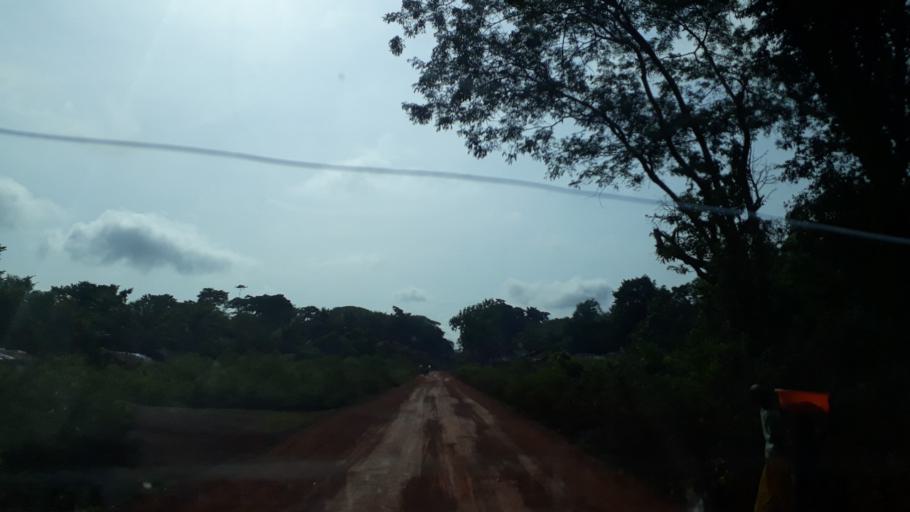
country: CD
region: Eastern Province
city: Wamba
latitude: 1.4032
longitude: 27.6586
